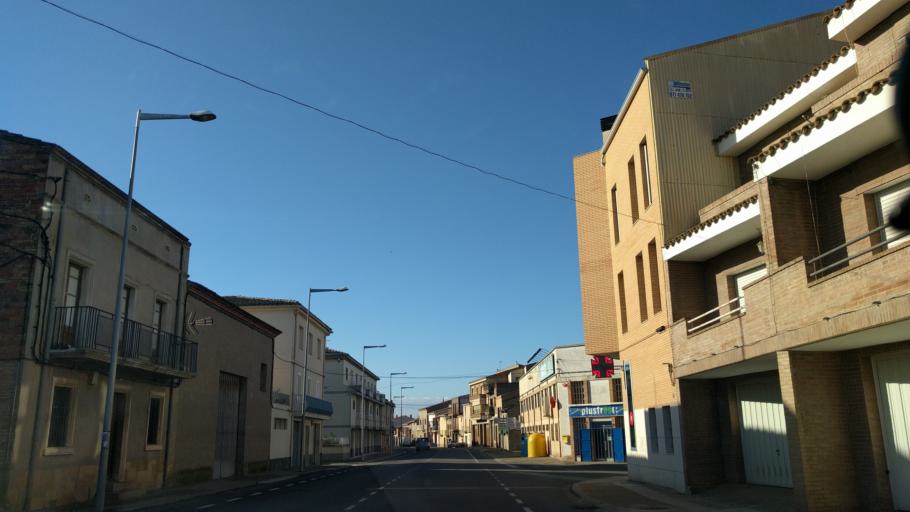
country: ES
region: Catalonia
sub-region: Provincia de Lleida
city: Corbins
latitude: 41.6887
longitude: 0.7280
